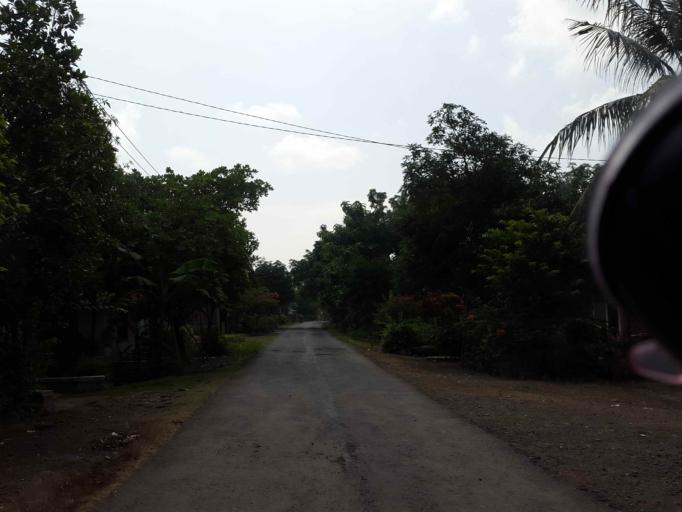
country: ID
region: Central Java
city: Pemalang
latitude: -6.9478
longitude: 109.3433
